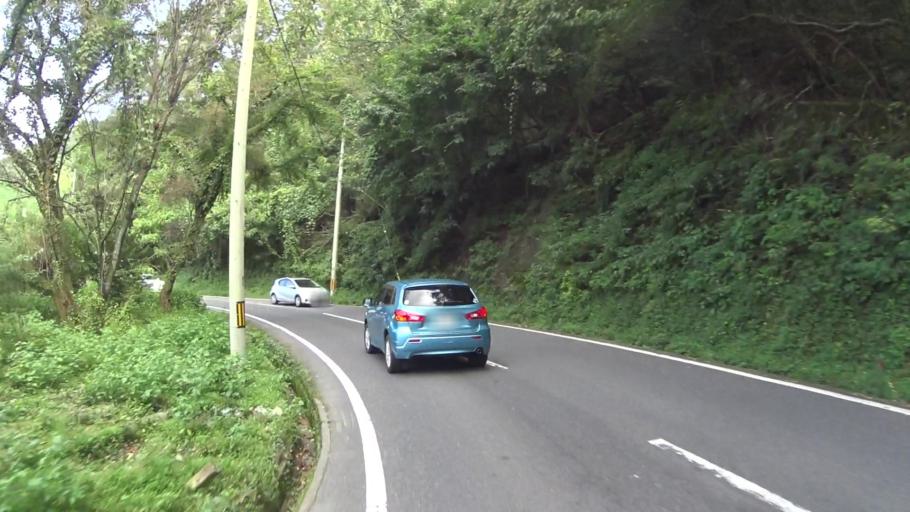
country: JP
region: Kyoto
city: Uji
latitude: 34.9126
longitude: 135.8694
